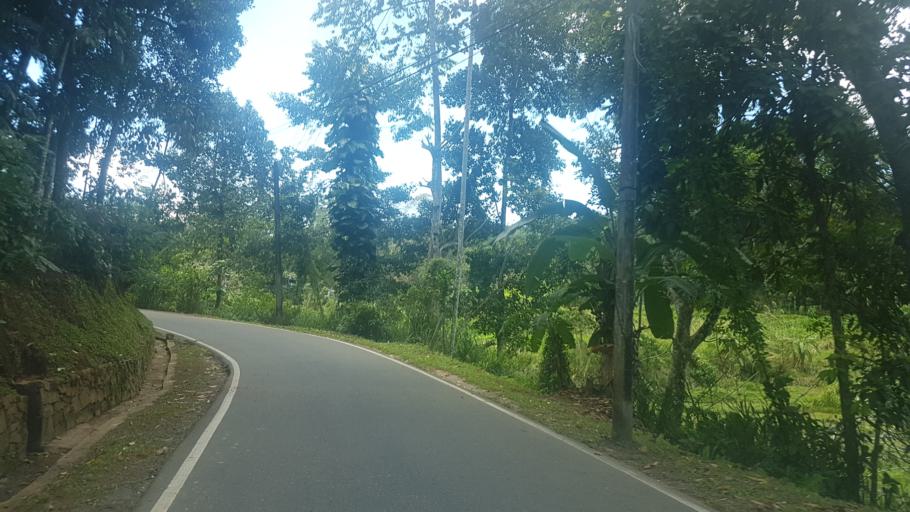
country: LK
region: Central
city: Gampola
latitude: 7.2165
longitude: 80.5900
